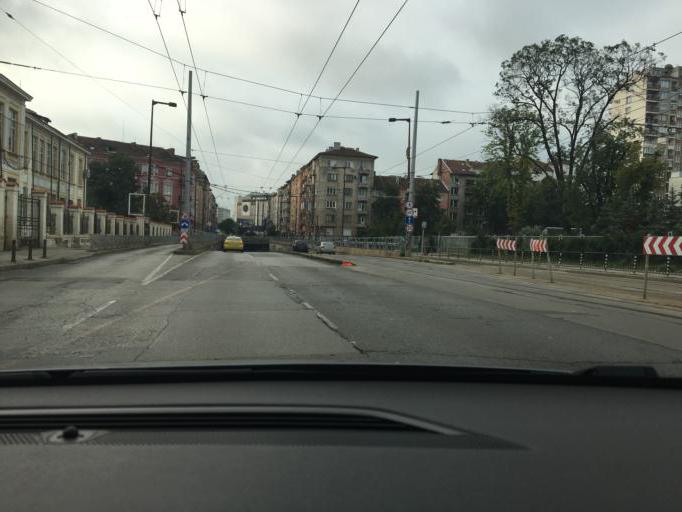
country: BG
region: Sofia-Capital
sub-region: Stolichna Obshtina
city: Sofia
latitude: 42.6886
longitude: 23.3151
